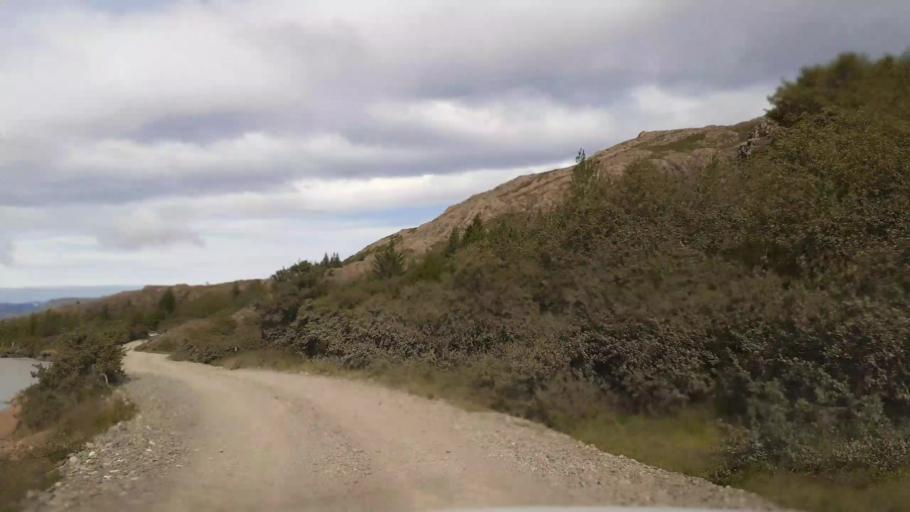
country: IS
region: East
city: Hoefn
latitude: 64.4371
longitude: -14.9086
